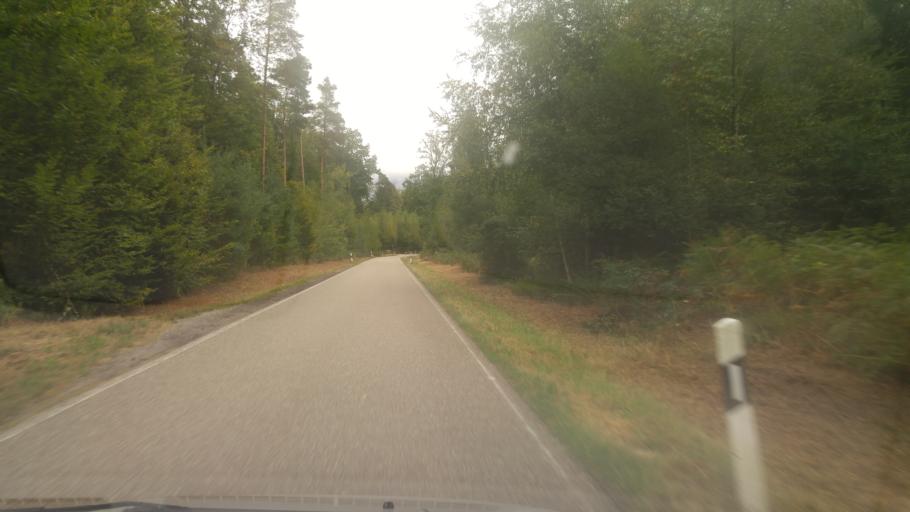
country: DE
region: Rheinland-Pfalz
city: Scheibenhardt
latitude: 48.9923
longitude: 8.1021
